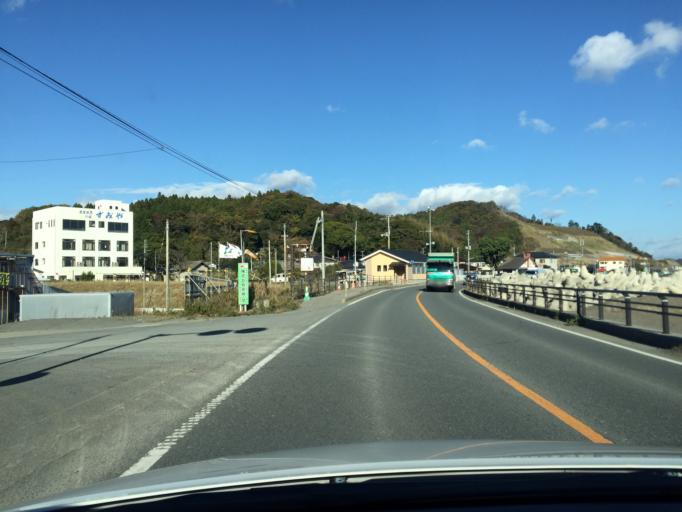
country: JP
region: Fukushima
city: Iwaki
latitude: 37.1195
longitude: 140.9977
